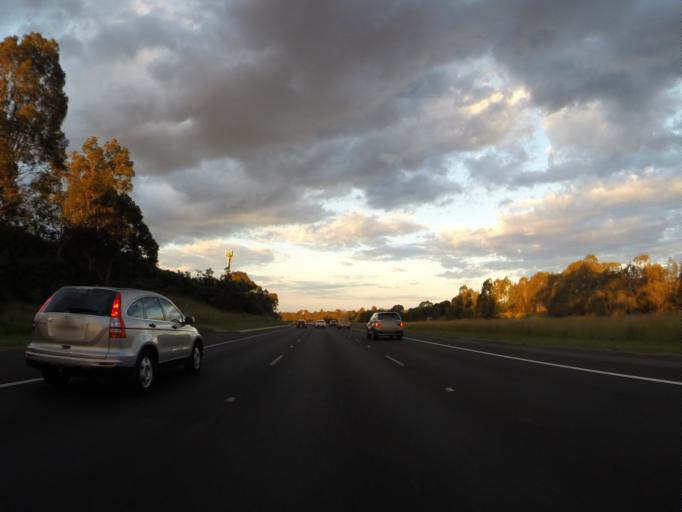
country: AU
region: New South Wales
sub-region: Campbelltown Municipality
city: Campbelltown
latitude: -34.0524
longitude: 150.8098
